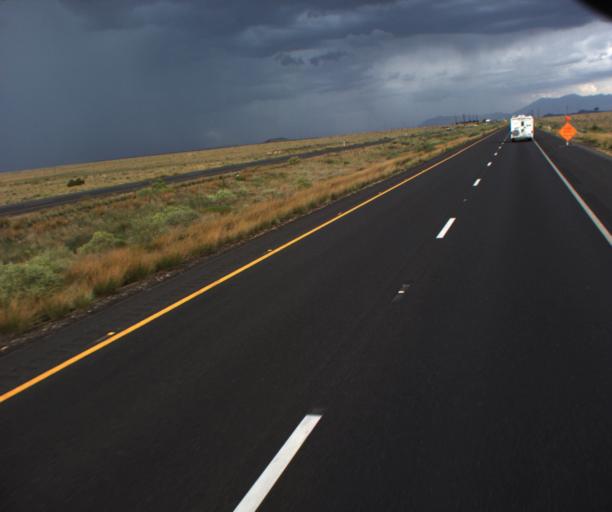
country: US
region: Arizona
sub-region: Coconino County
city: Flagstaff
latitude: 35.1514
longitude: -111.2442
